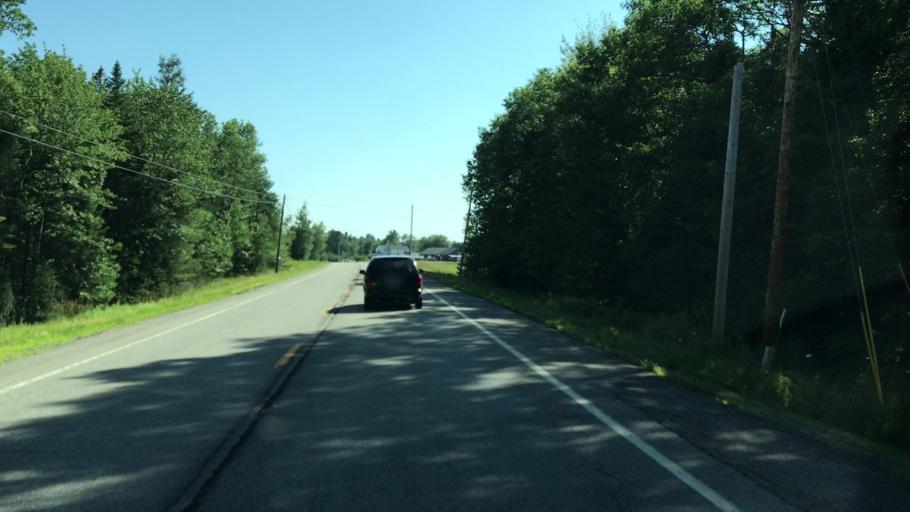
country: US
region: Maine
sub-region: Penobscot County
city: Enfield
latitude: 45.3006
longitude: -68.6170
